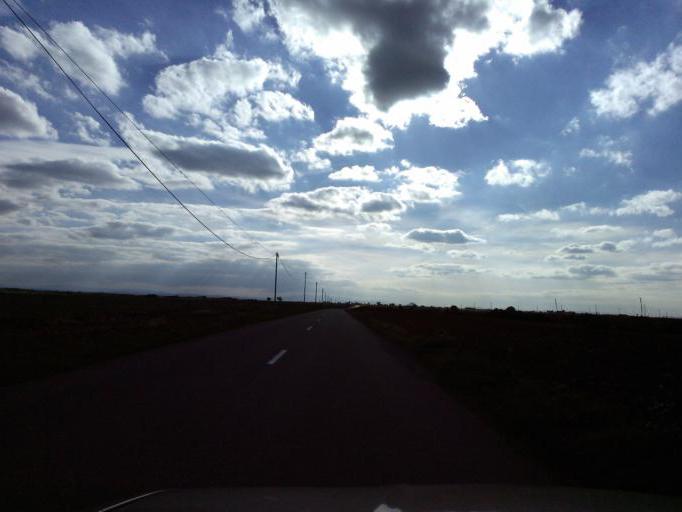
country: FR
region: Provence-Alpes-Cote d'Azur
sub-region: Departement des Alpes-de-Haute-Provence
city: Valensole
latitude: 43.8764
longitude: 6.0260
